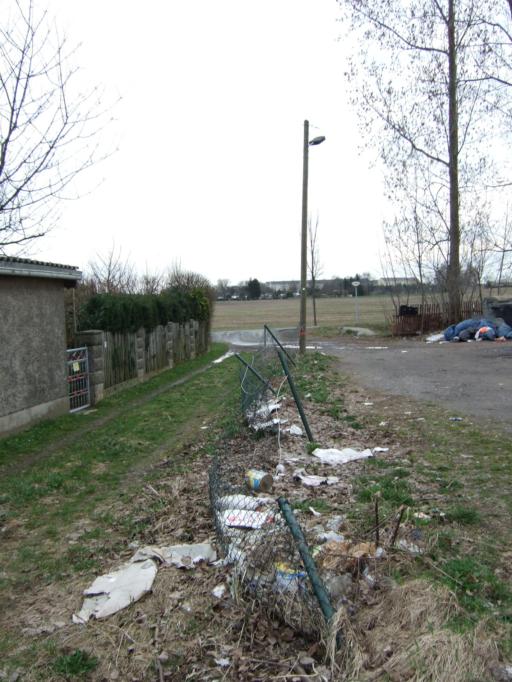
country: DE
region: Saxony
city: Brand-Erbisdorf
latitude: 50.8677
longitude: 13.3362
